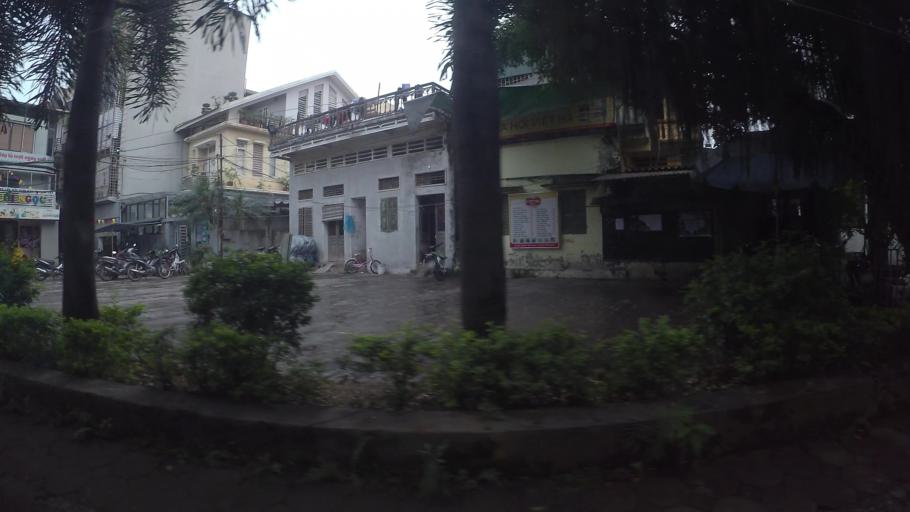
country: VN
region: Ha Noi
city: Van Dien
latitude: 20.9699
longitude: 105.8706
